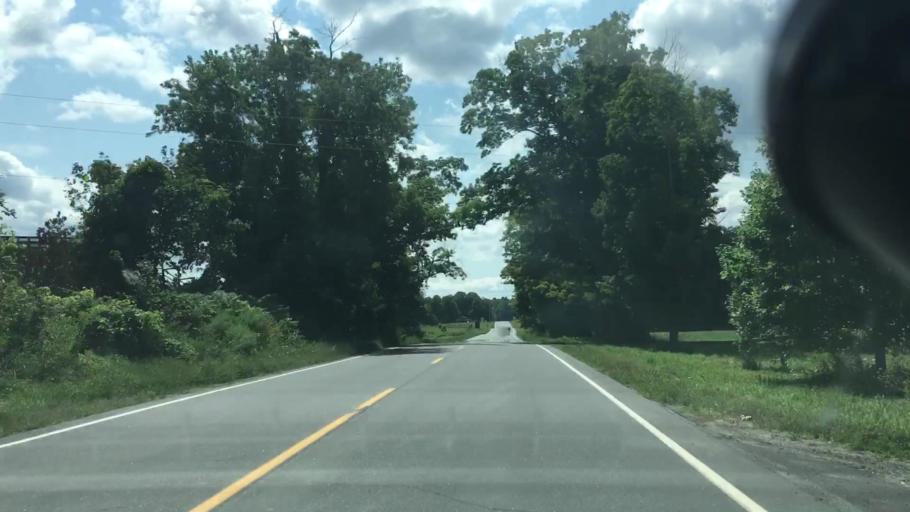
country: US
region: Maine
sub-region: Somerset County
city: Fairfield
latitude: 44.6436
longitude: -69.6774
